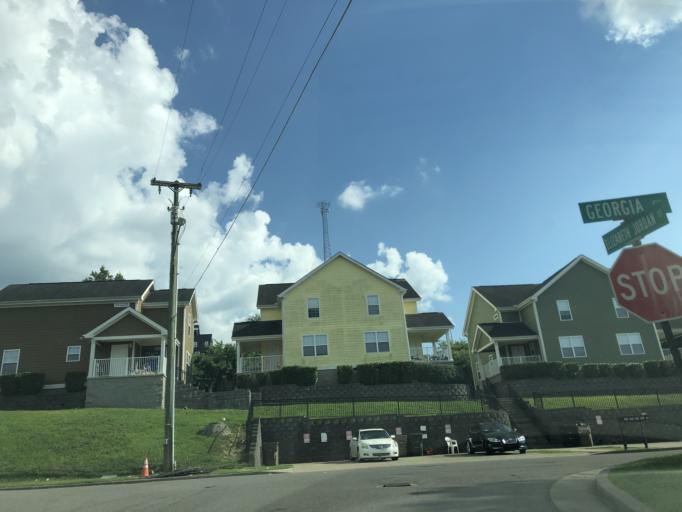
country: US
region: Tennessee
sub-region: Davidson County
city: Nashville
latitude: 36.1565
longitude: -86.8287
